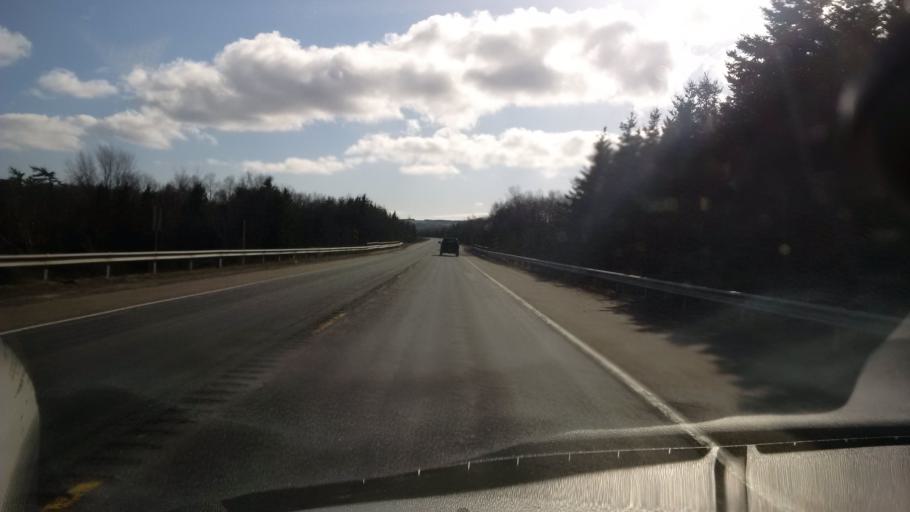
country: CA
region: Nova Scotia
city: Antigonish
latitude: 45.5780
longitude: -62.1043
